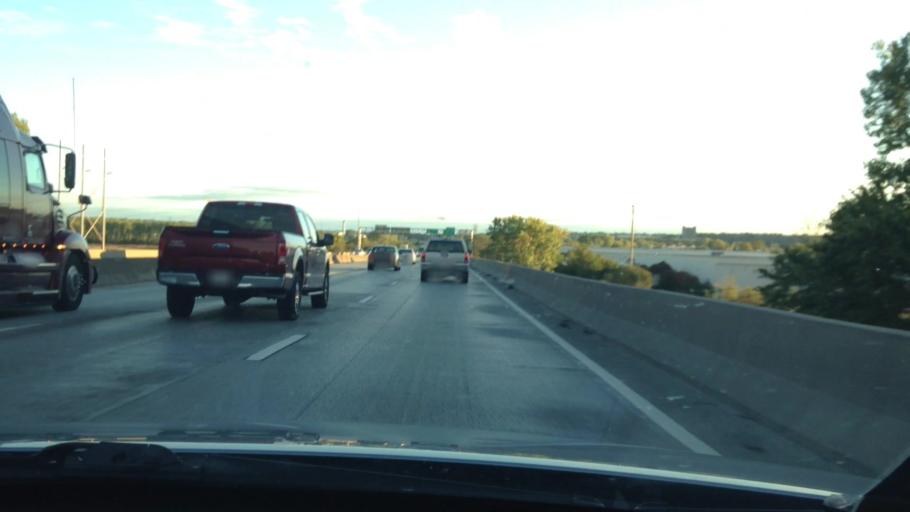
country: US
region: Missouri
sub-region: Clay County
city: Claycomo
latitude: 39.1475
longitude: -94.4985
